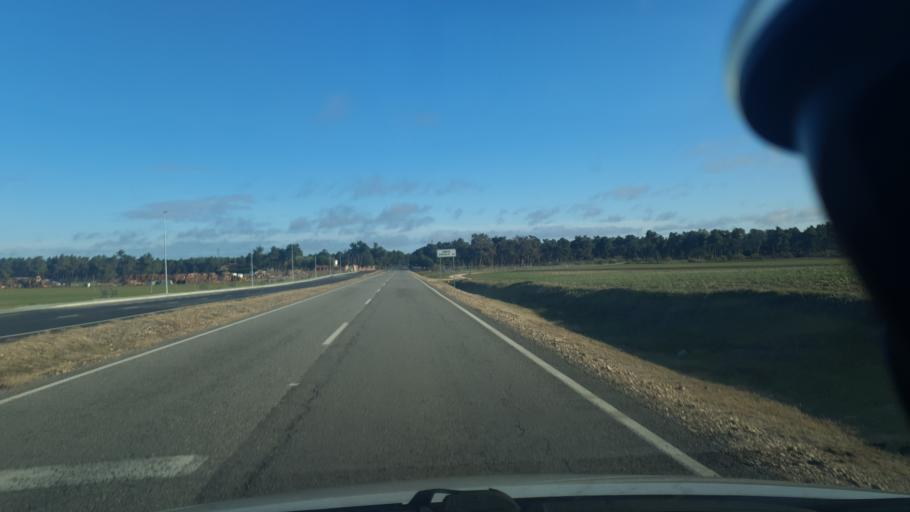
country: ES
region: Castille and Leon
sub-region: Provincia de Avila
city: Tinosillos
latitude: 40.9406
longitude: -4.7232
